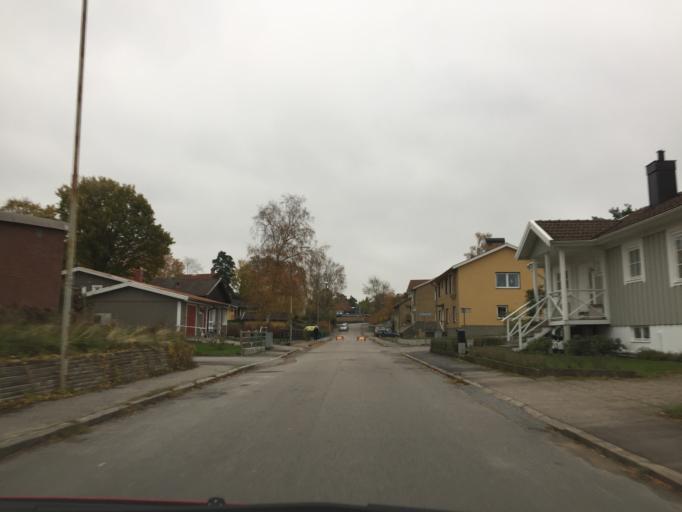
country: SE
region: Vaestra Goetaland
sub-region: Trollhattan
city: Trollhattan
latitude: 58.2668
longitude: 12.2784
